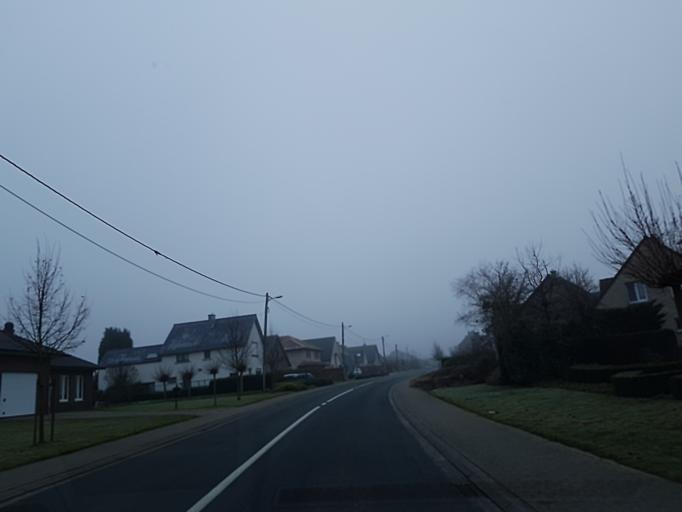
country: BE
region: Flanders
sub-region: Provincie Vlaams-Brabant
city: Meise
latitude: 50.9632
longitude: 4.3211
